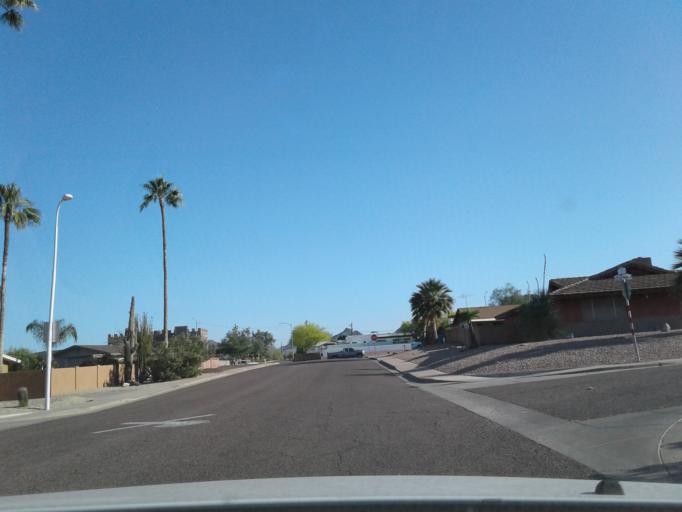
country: US
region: Arizona
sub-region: Maricopa County
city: Phoenix
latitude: 33.5373
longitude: -112.0387
